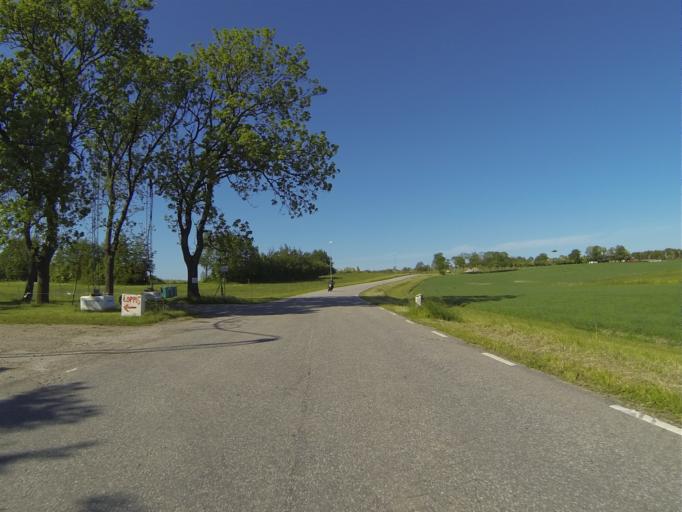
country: SE
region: Skane
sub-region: Malmo
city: Oxie
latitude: 55.5896
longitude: 13.1231
